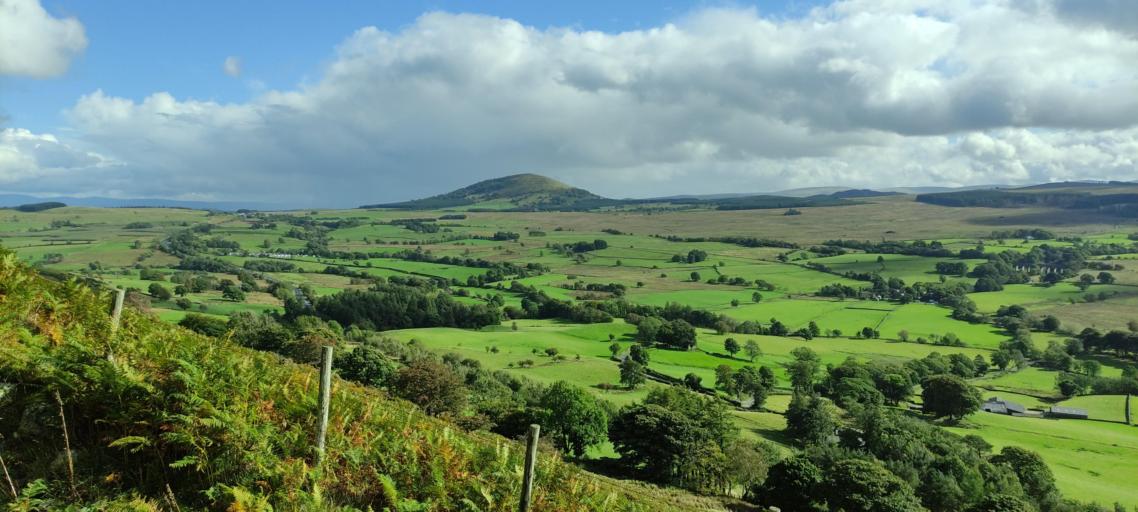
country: GB
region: England
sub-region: Cumbria
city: Keswick
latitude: 54.6350
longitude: -3.0172
